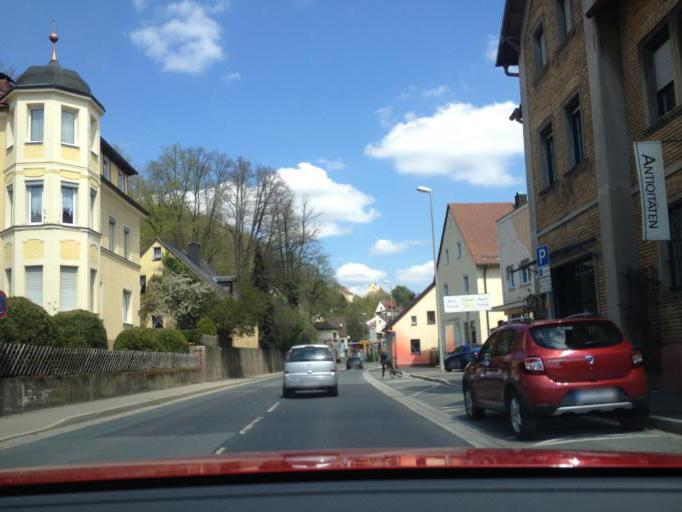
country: DE
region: Bavaria
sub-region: Upper Franconia
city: Pegnitz
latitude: 49.7556
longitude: 11.5364
